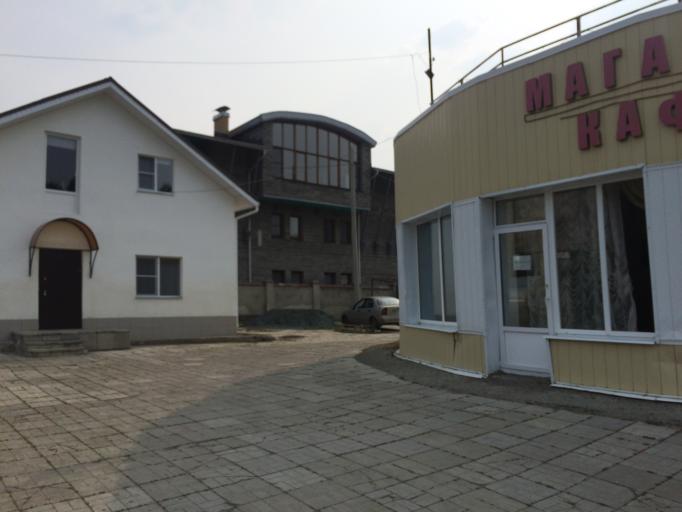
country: RU
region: Bashkortostan
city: Abzakovo
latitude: 53.8110
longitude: 58.6367
